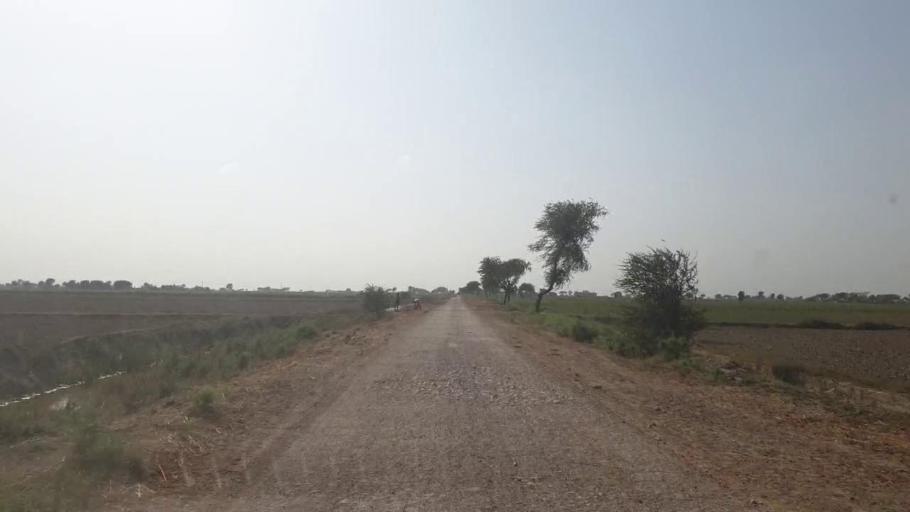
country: PK
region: Sindh
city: Kario
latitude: 24.5589
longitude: 68.5110
